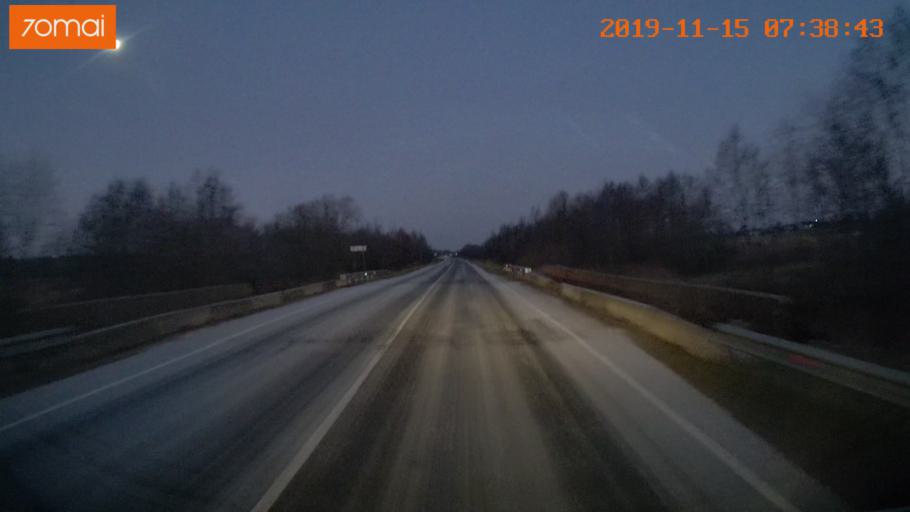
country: RU
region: Vologda
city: Sheksna
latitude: 58.7600
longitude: 38.3965
